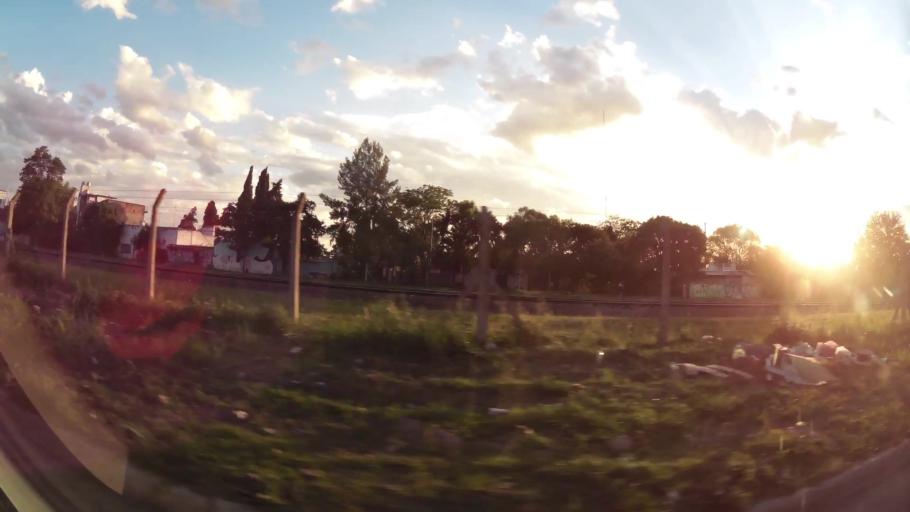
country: AR
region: Buenos Aires
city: Santa Catalina - Dique Lujan
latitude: -34.4697
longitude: -58.7599
